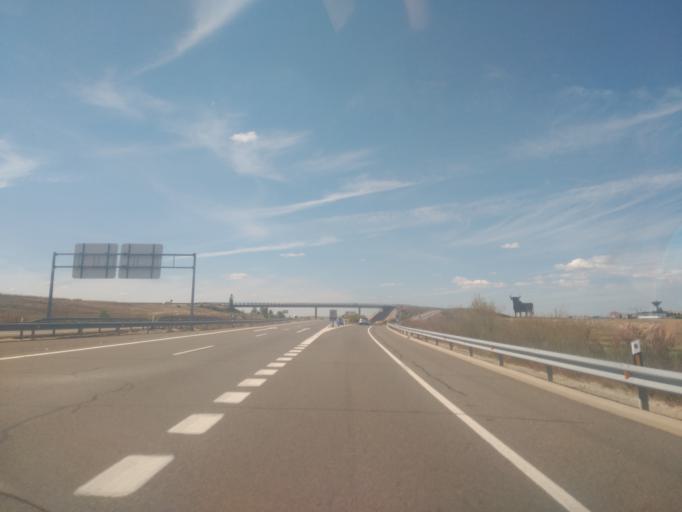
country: ES
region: Castille and Leon
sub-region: Provincia de Salamanca
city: Carbajosa de la Sagrada
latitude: 40.9204
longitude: -5.6659
